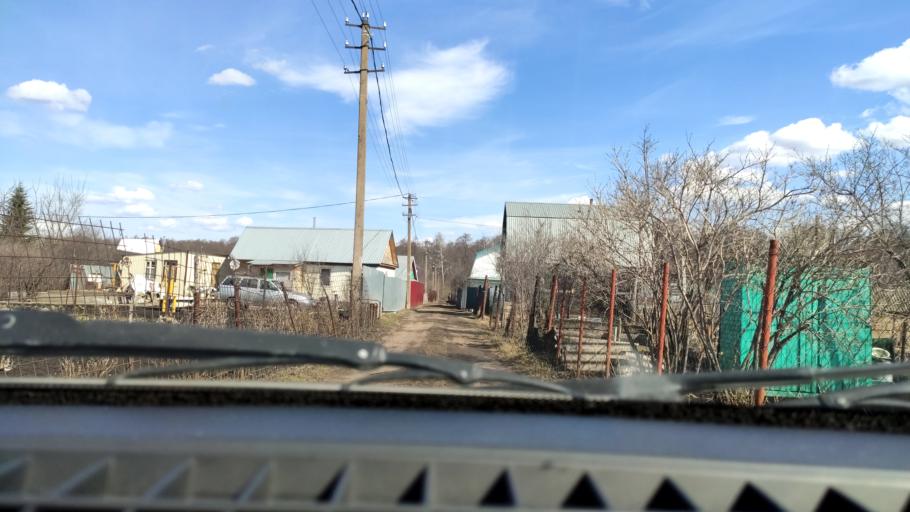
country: RU
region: Bashkortostan
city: Avdon
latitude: 54.6791
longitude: 55.8197
